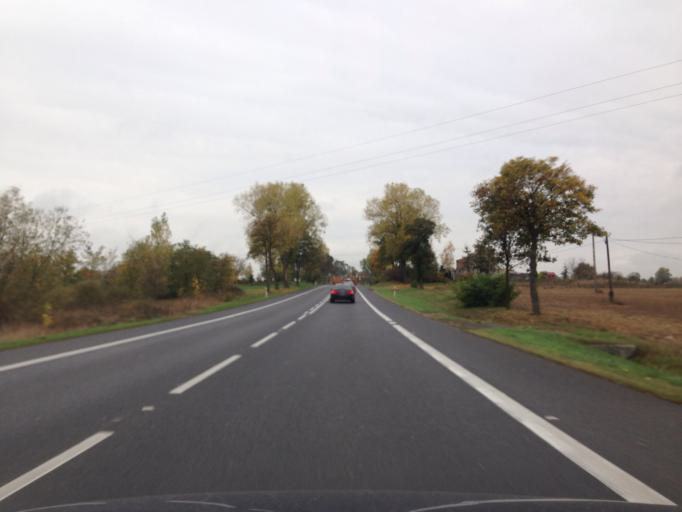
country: PL
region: Kujawsko-Pomorskie
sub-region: Powiat swiecki
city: Pruszcz
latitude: 53.3144
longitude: 18.2697
